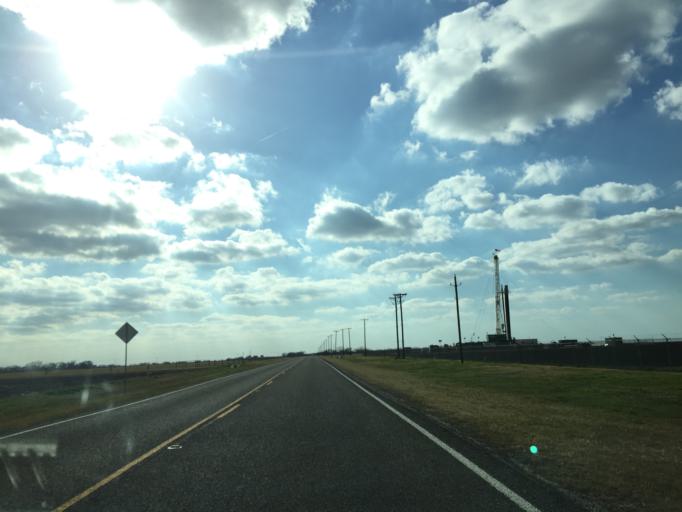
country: US
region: Texas
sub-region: Williamson County
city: Granger
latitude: 30.6543
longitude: -97.3823
